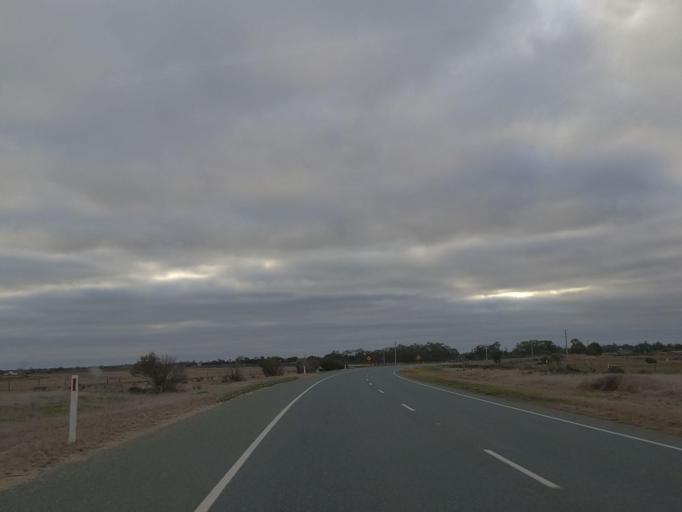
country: AU
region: Victoria
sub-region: Swan Hill
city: Swan Hill
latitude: -35.6246
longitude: 143.8059
